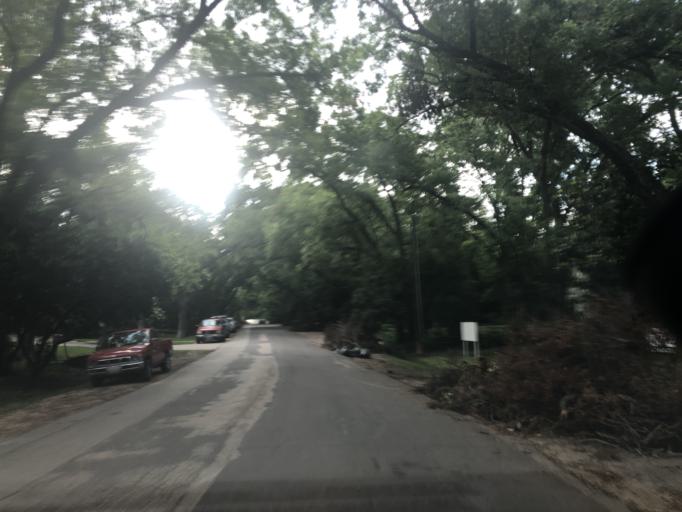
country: US
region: Texas
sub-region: Dallas County
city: University Park
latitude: 32.8584
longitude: -96.8410
